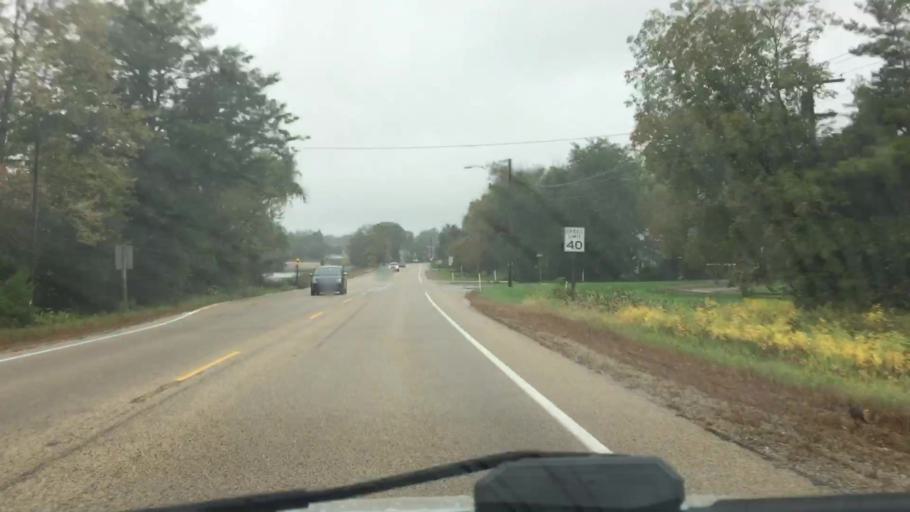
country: US
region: Wisconsin
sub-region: Jefferson County
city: Palmyra
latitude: 42.8822
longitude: -88.5757
